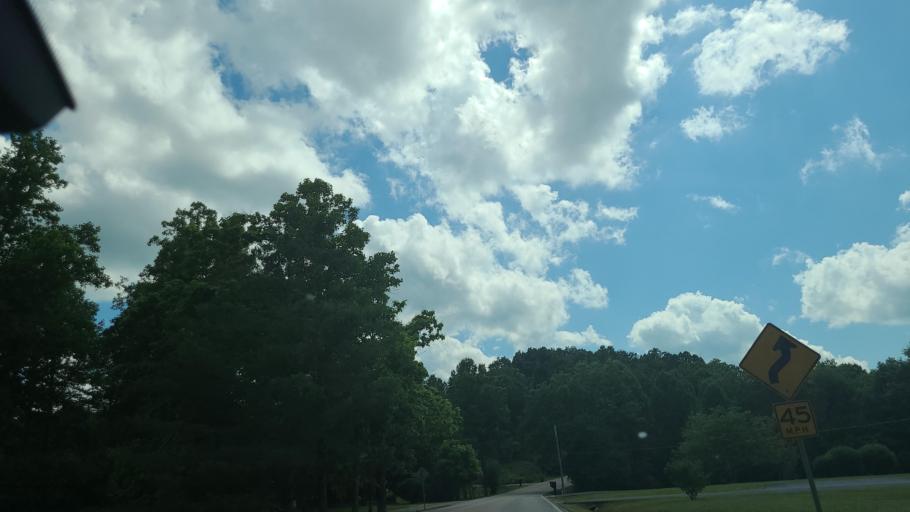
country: US
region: Kentucky
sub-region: Whitley County
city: Williamsburg
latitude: 36.8462
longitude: -84.2414
